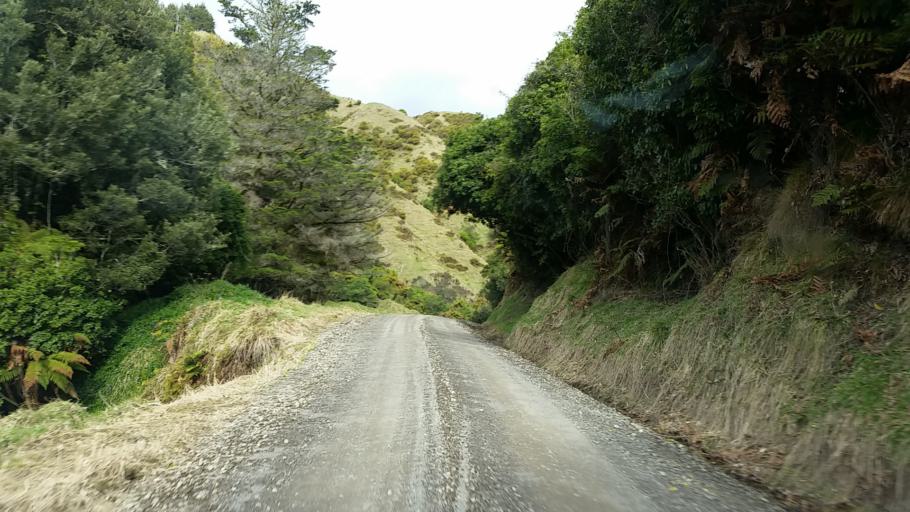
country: NZ
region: Taranaki
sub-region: South Taranaki District
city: Eltham
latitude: -39.1709
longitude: 174.6104
